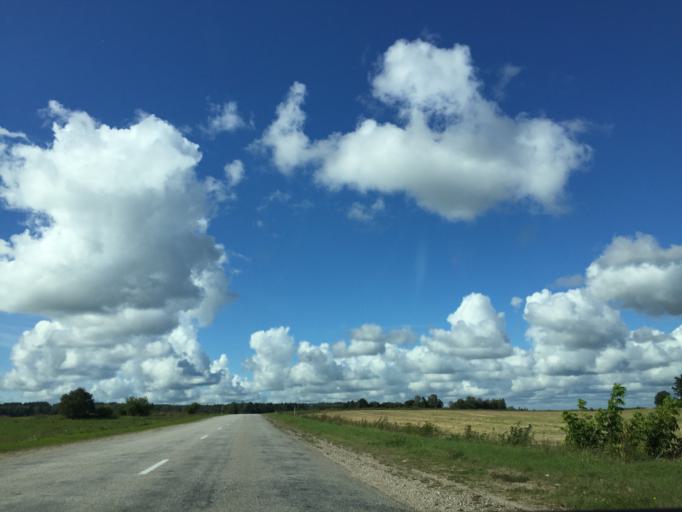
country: LV
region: Kuldigas Rajons
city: Kuldiga
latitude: 56.9662
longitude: 21.9115
